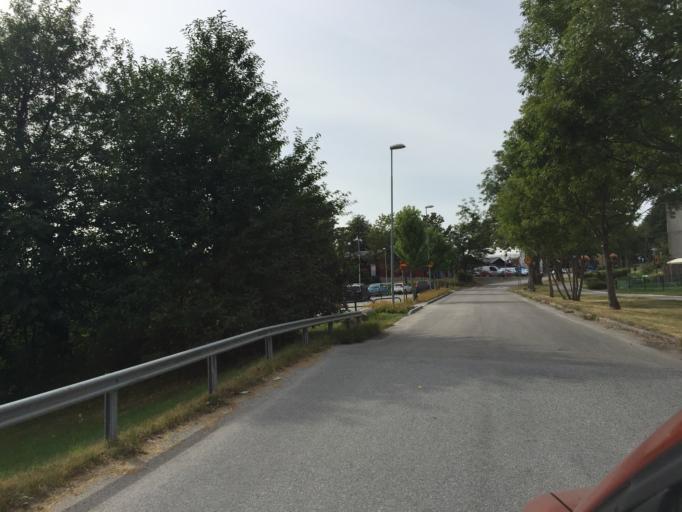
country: SE
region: Stockholm
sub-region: Botkyrka Kommun
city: Fittja
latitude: 59.2483
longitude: 17.8686
